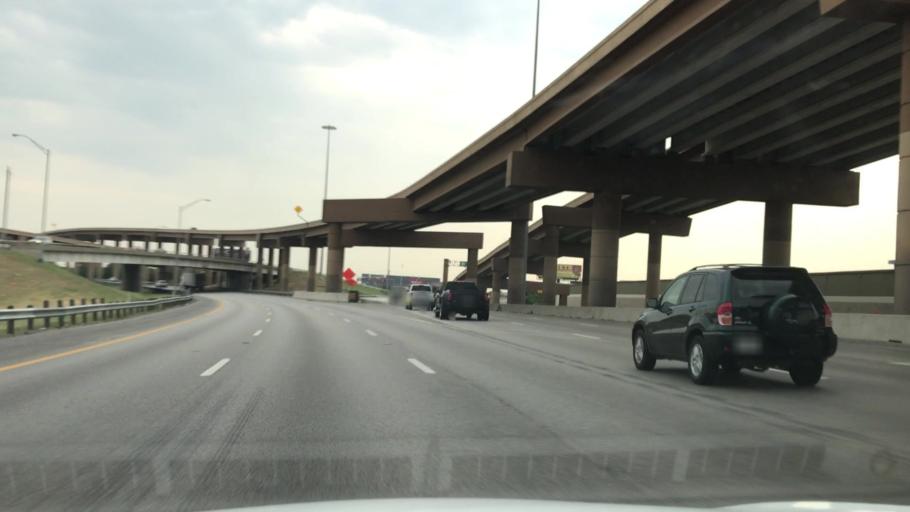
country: US
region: Texas
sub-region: Dallas County
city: Farmers Branch
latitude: 32.8713
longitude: -96.8986
